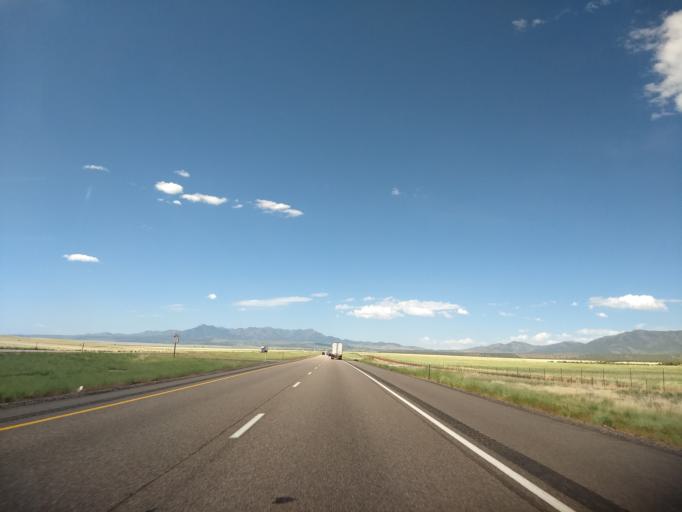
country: US
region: Utah
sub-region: Millard County
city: Fillmore
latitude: 39.0233
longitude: -112.3024
